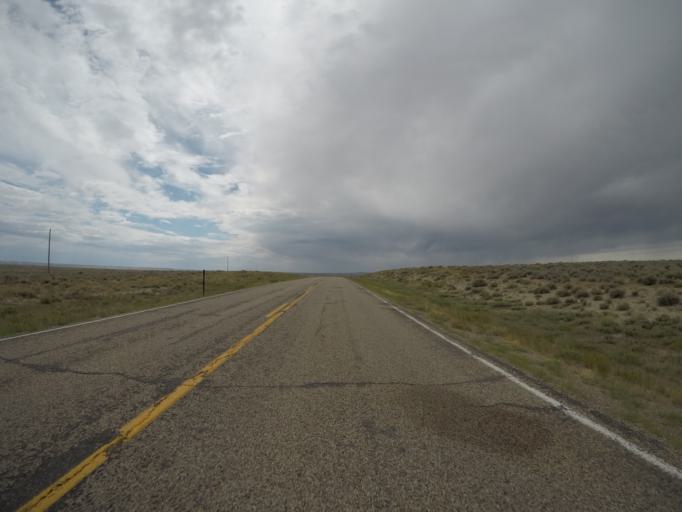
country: US
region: Wyoming
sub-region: Lincoln County
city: Kemmerer
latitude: 41.9656
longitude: -110.0946
